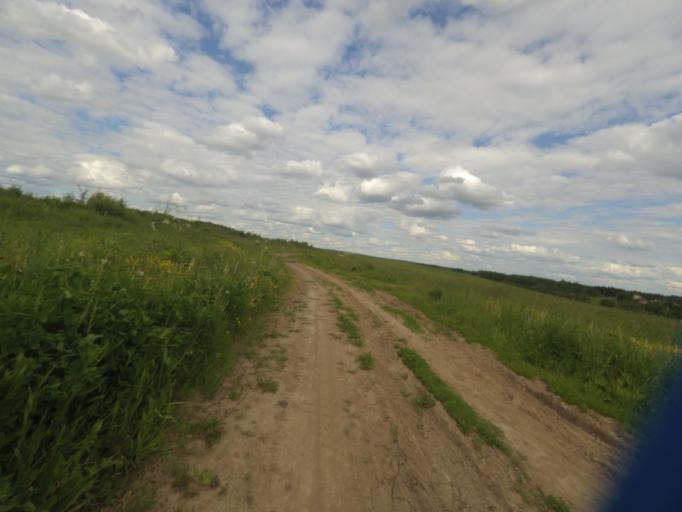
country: RU
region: Moskovskaya
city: Marfino
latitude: 56.1070
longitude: 37.5762
